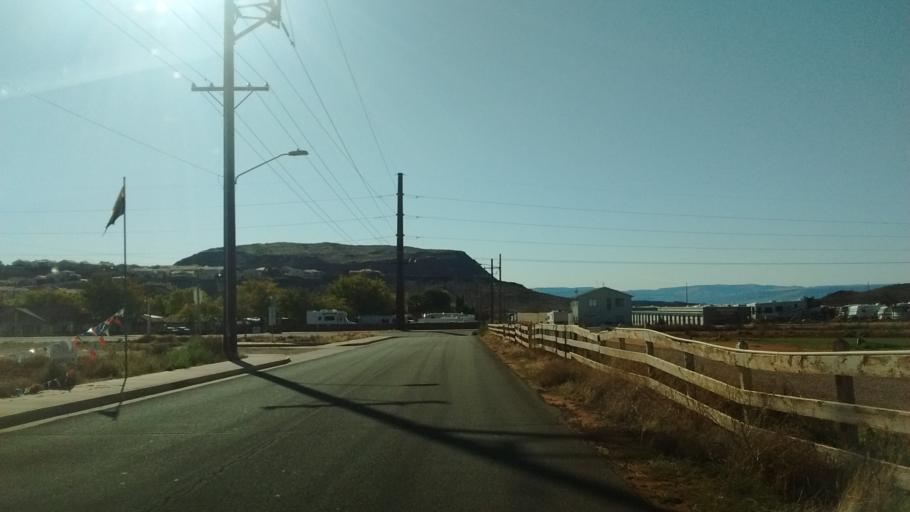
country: US
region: Utah
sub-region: Washington County
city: Washington
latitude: 37.1318
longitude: -113.4909
